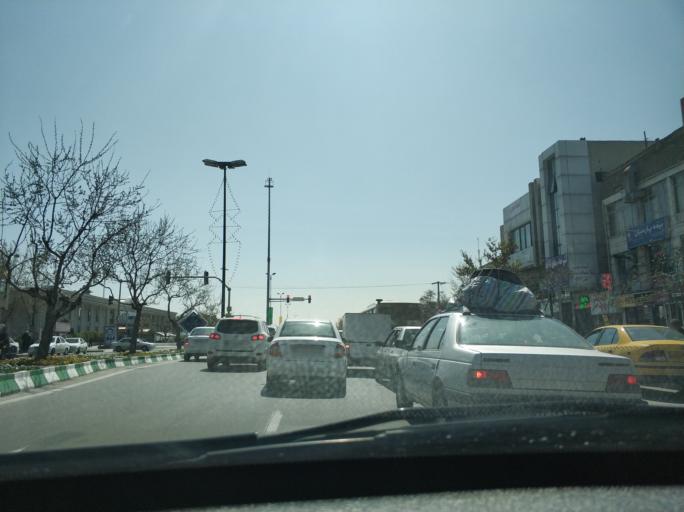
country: IR
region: Razavi Khorasan
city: Mashhad
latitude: 36.2583
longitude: 59.6083
